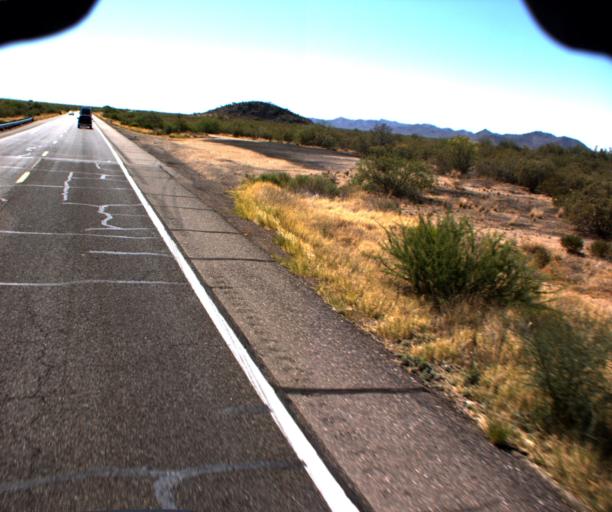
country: US
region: Arizona
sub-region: Yavapai County
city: Congress
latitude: 34.1774
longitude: -113.0301
